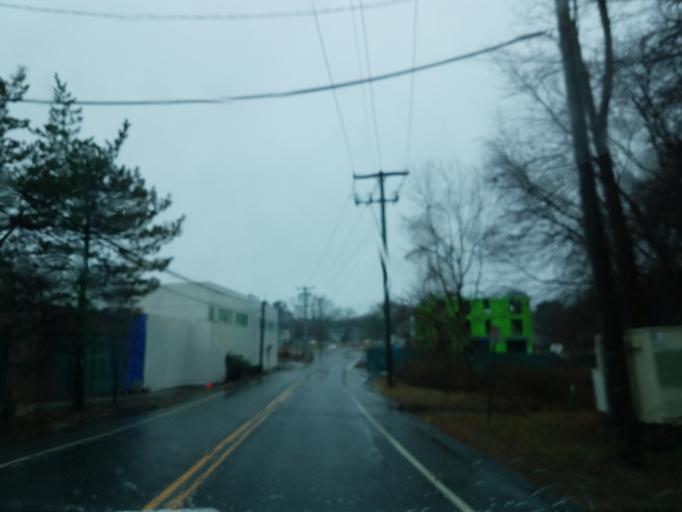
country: US
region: Connecticut
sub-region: Fairfield County
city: Westport
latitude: 41.1385
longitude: -73.3365
